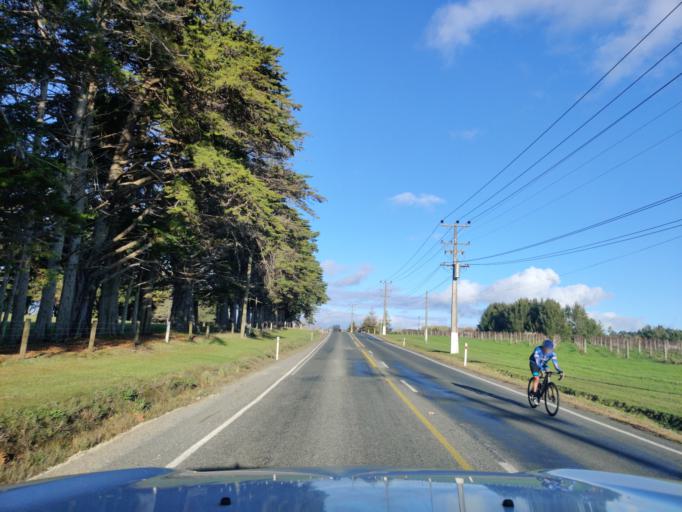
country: NZ
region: Auckland
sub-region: Auckland
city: Pakuranga
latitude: -36.9566
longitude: 174.9701
